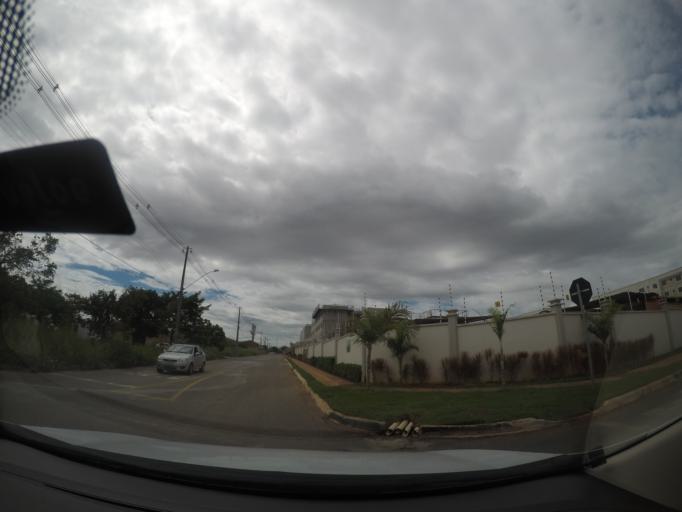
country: BR
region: Goias
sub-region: Goiania
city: Goiania
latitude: -16.7286
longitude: -49.3428
